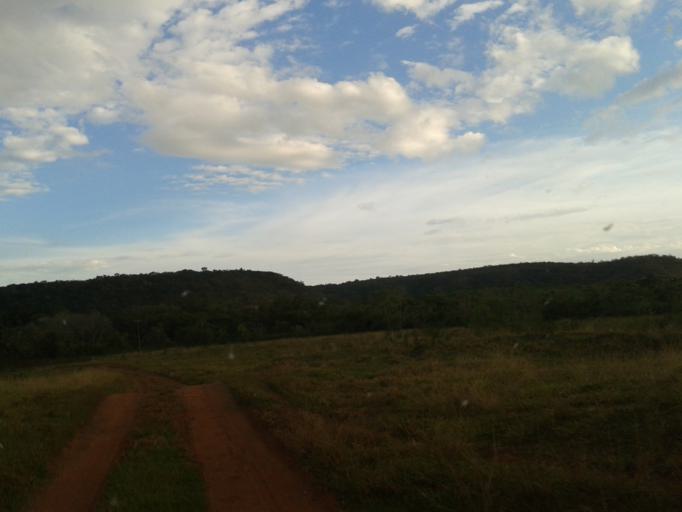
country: BR
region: Minas Gerais
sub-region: Campina Verde
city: Campina Verde
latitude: -19.3523
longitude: -49.6677
